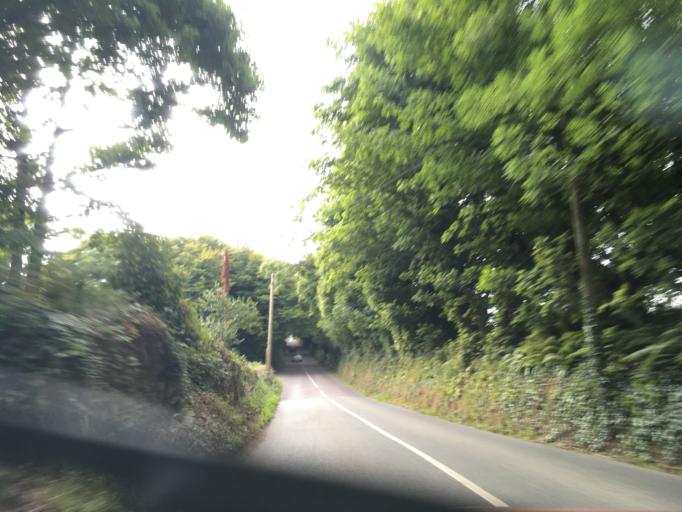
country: IE
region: Munster
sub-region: County Cork
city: Crosshaven
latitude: 51.7963
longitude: -8.2991
